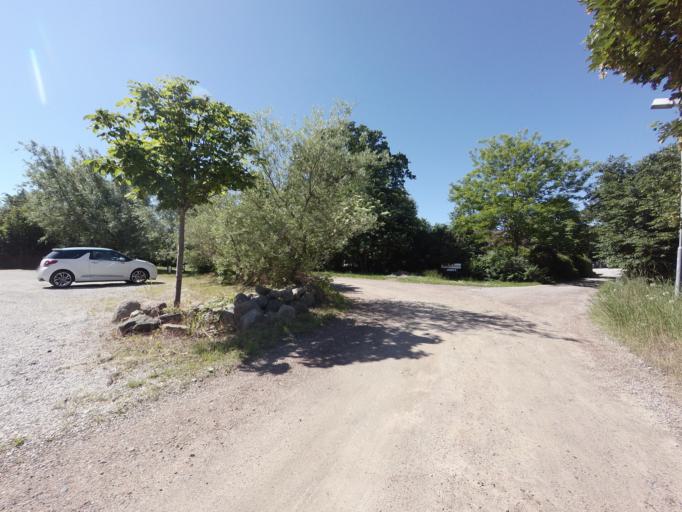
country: SE
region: Skane
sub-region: Vellinge Kommun
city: Hollviken
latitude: 55.4028
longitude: 12.9907
